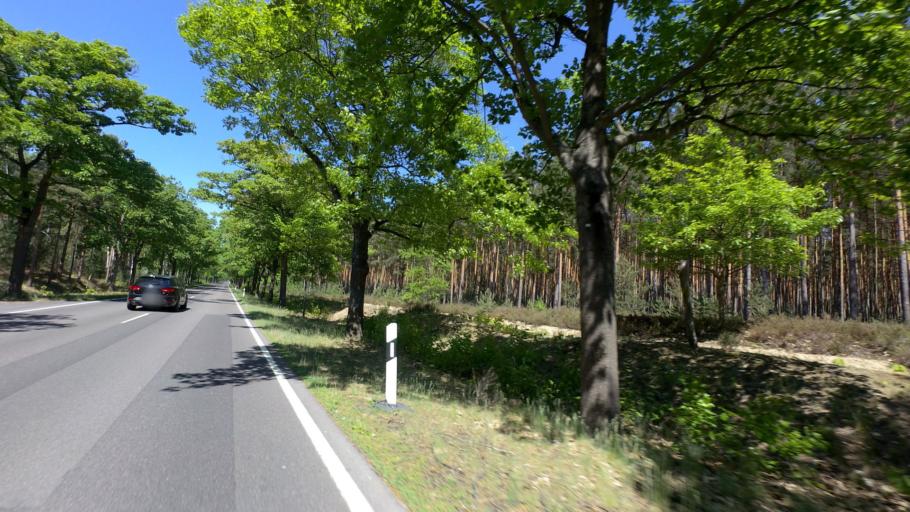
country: DE
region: Brandenburg
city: Drachhausen
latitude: 51.9234
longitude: 14.3475
